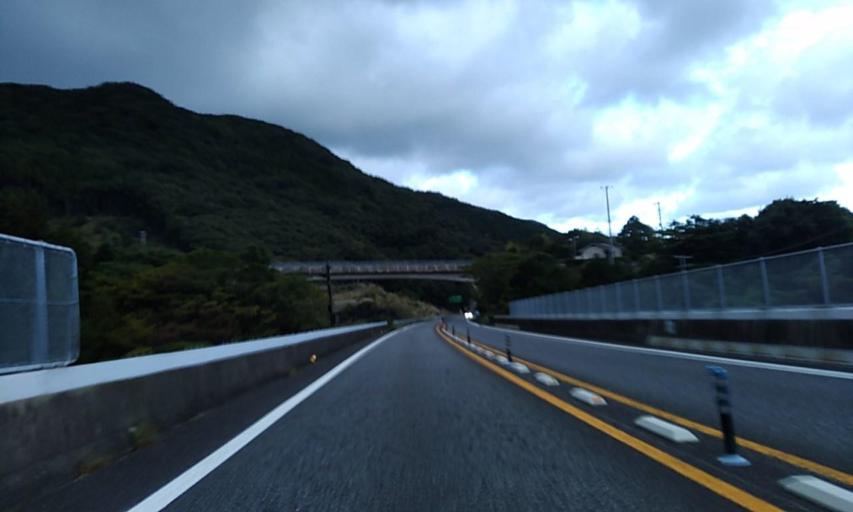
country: JP
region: Wakayama
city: Shingu
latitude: 33.6860
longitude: 135.9546
